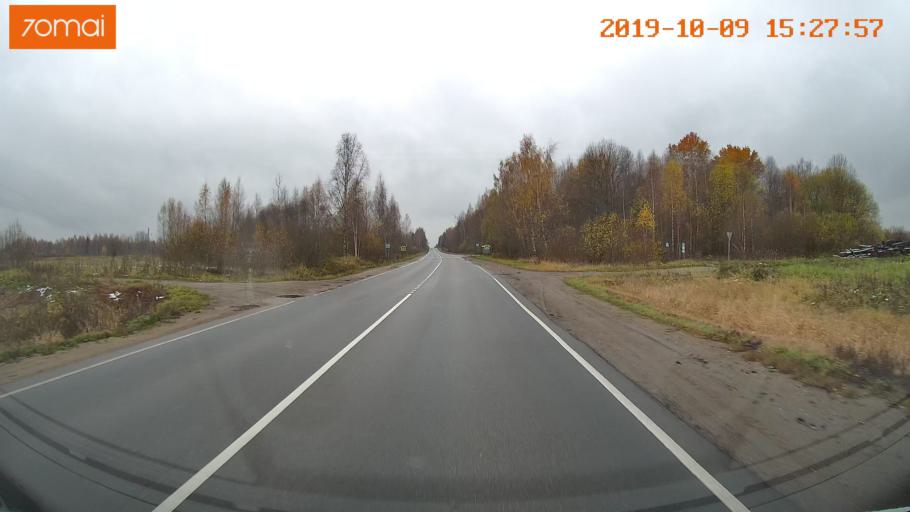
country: RU
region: Kostroma
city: Susanino
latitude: 58.0087
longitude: 41.3682
